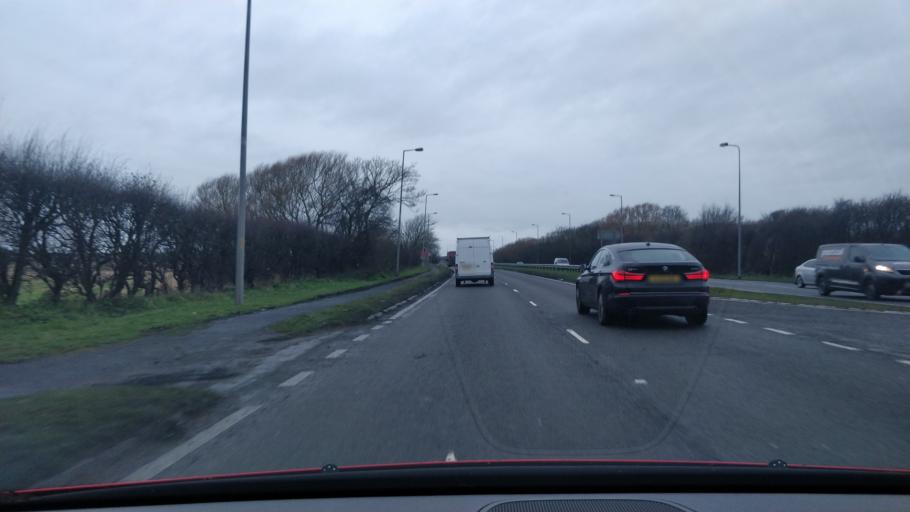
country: GB
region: England
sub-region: Sefton
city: Ince Blundell
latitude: 53.5338
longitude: -3.0415
